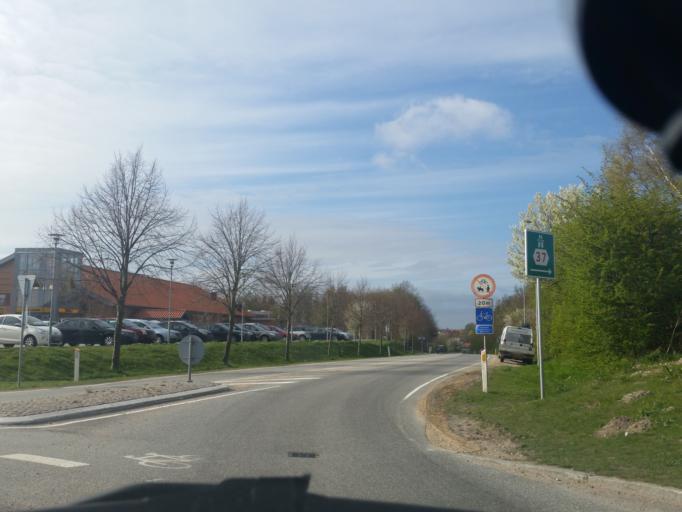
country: DK
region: Zealand
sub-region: Soro Kommune
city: Soro
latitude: 55.4455
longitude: 11.5644
